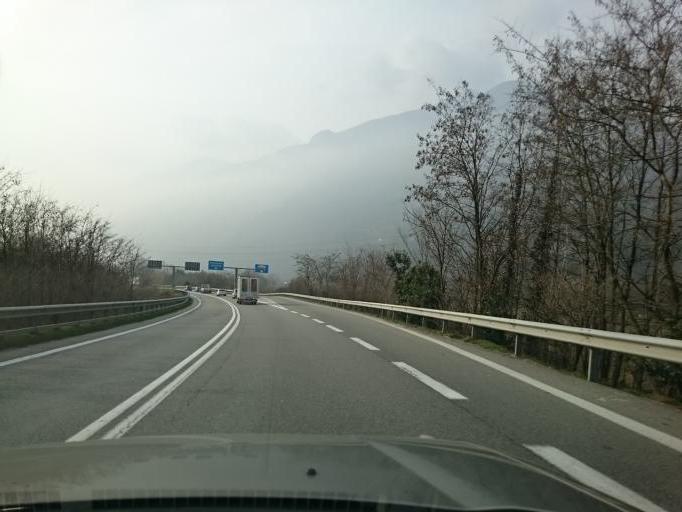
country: IT
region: Lombardy
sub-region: Provincia di Brescia
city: Gianico
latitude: 45.8723
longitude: 10.1651
